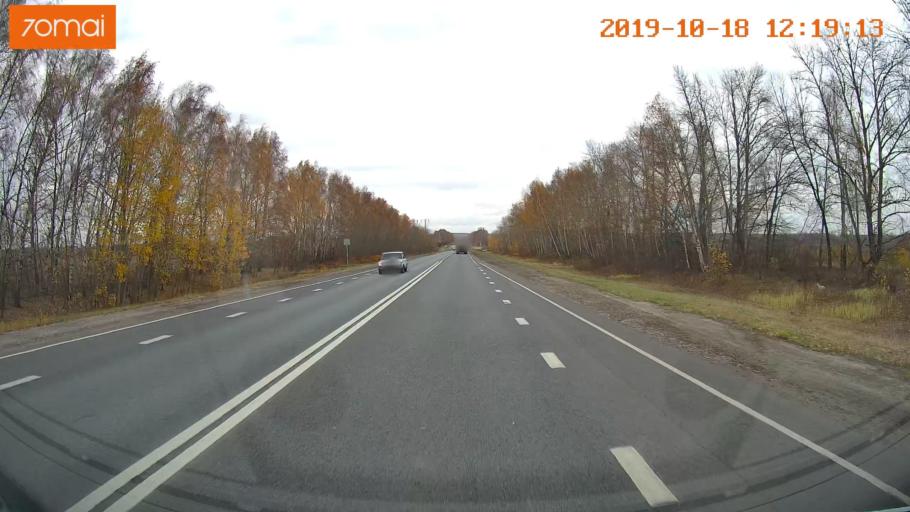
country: RU
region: Rjazan
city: Zakharovo
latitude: 54.4791
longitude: 39.4656
